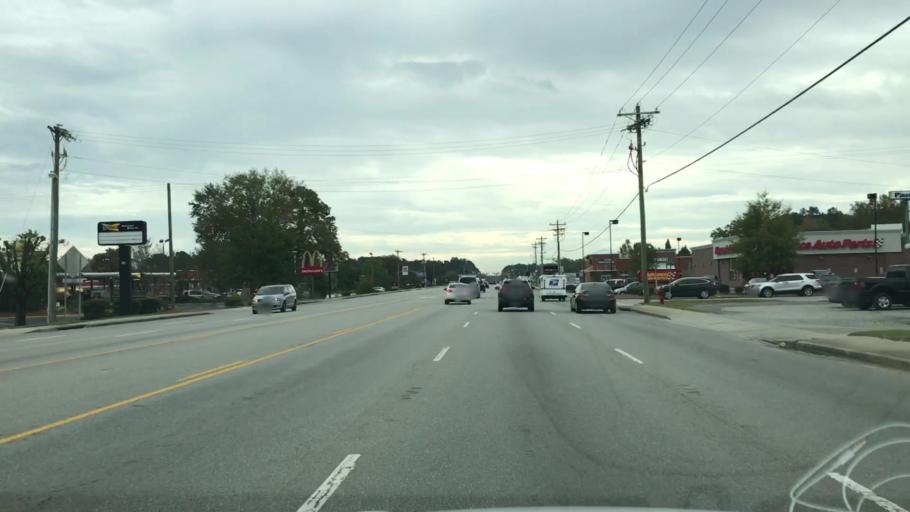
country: US
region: South Carolina
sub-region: Berkeley County
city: Goose Creek
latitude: 32.9999
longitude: -80.0409
